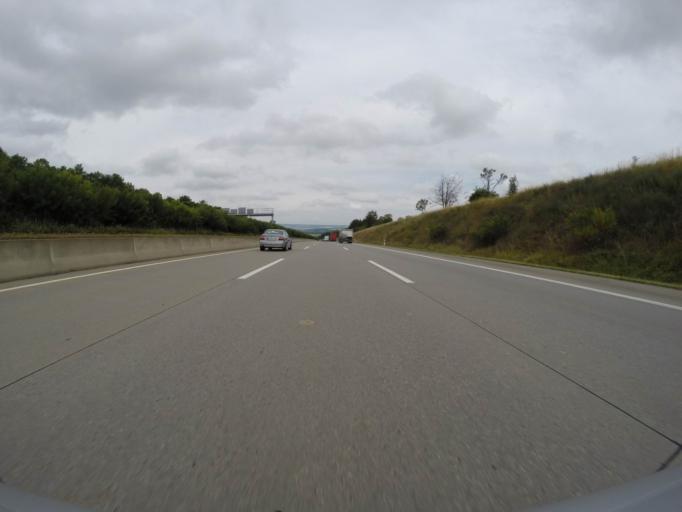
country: DE
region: Thuringia
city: Mellingen
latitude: 50.9182
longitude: 11.4085
